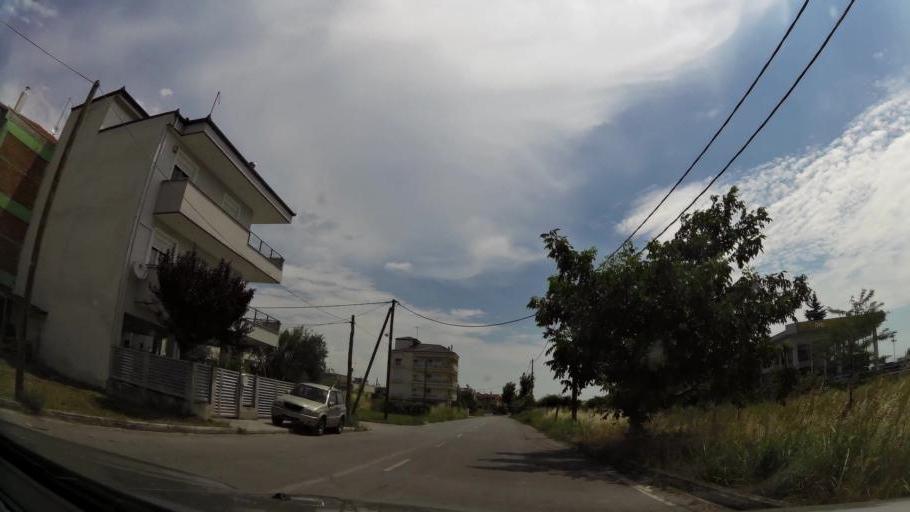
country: GR
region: Central Macedonia
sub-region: Nomos Pierias
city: Katerini
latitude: 40.2587
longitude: 22.5096
